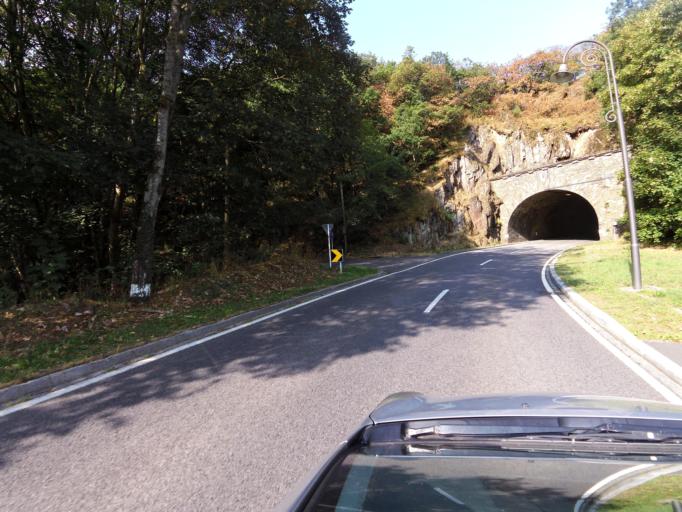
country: LU
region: Diekirch
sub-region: Canton de Diekirch
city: Bourscheid
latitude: 49.9122
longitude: 6.0815
